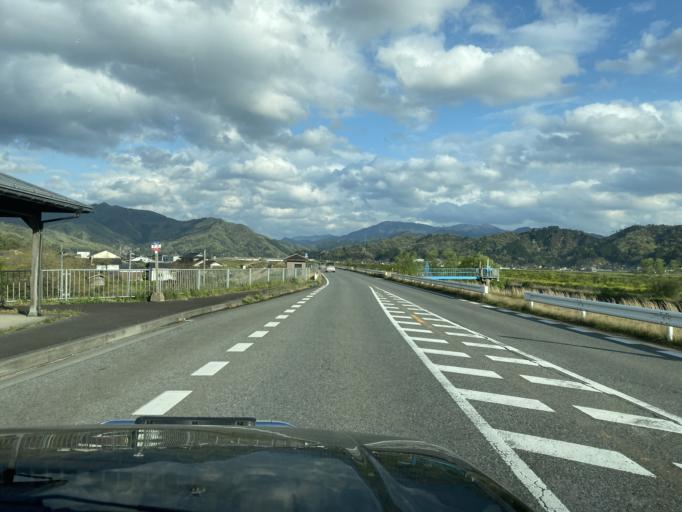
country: JP
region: Hyogo
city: Toyooka
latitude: 35.4921
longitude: 134.8425
